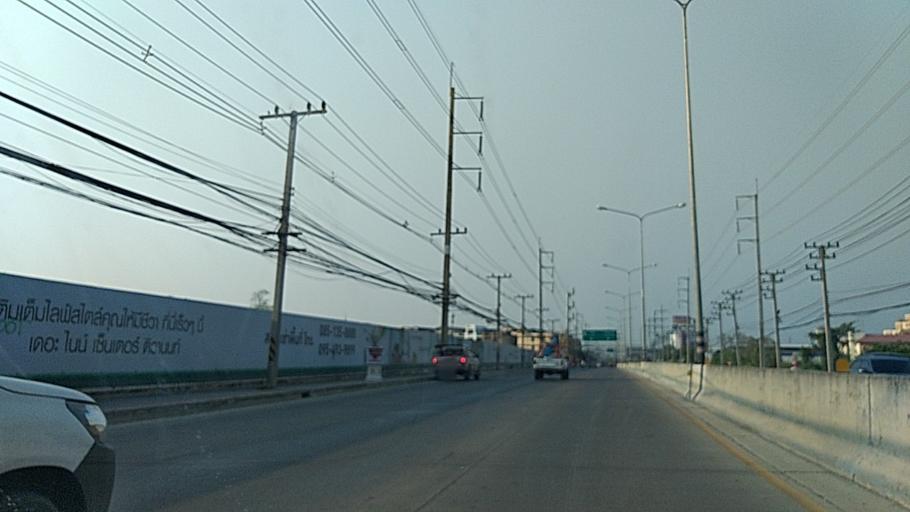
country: TH
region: Phra Nakhon Si Ayutthaya
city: Ban Bang Kadi Pathum Thani
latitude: 13.9786
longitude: 100.5506
